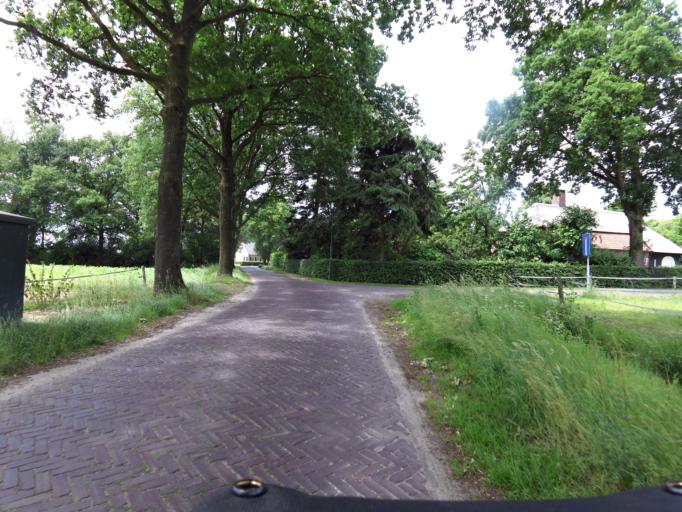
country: NL
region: North Brabant
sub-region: Gemeente Bladel en Netersel
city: Bladel
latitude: 51.3827
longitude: 5.1871
